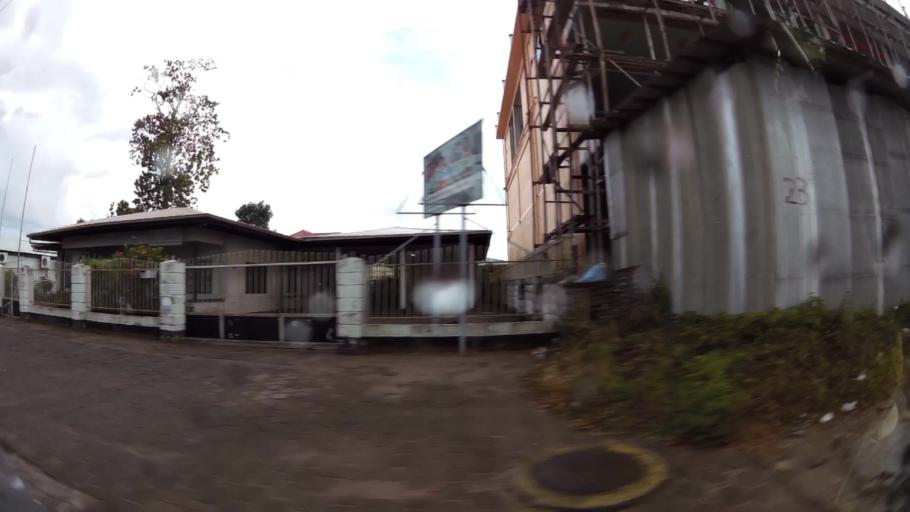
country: SR
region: Paramaribo
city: Paramaribo
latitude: 5.8144
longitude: -55.1828
